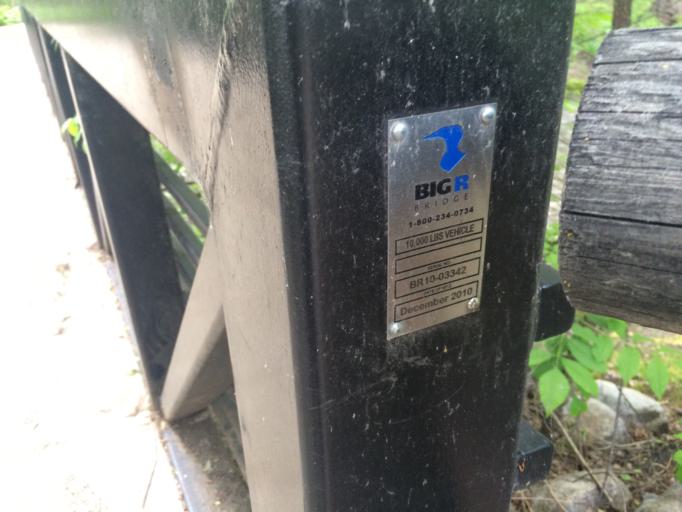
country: US
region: Colorado
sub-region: Boulder County
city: Boulder
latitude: 40.0193
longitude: -105.2359
